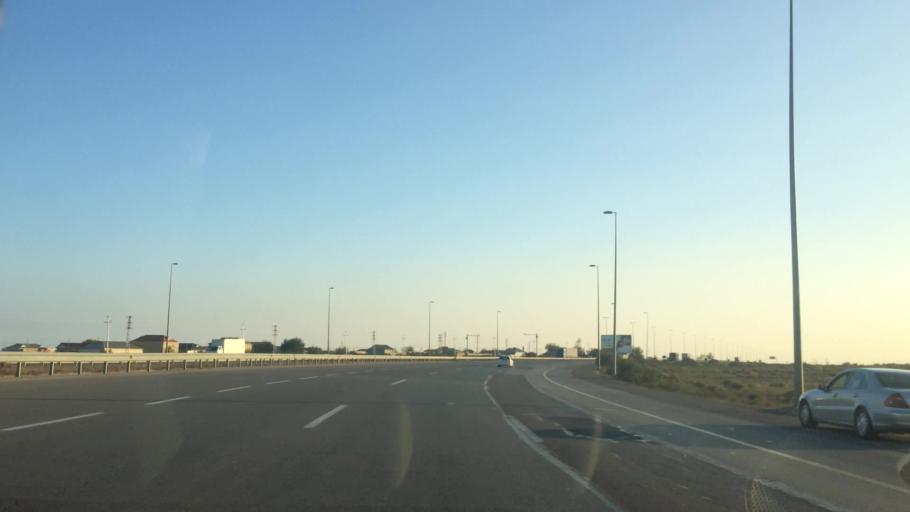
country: AZ
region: Baki
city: Qobustan
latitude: 39.9924
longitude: 49.4304
